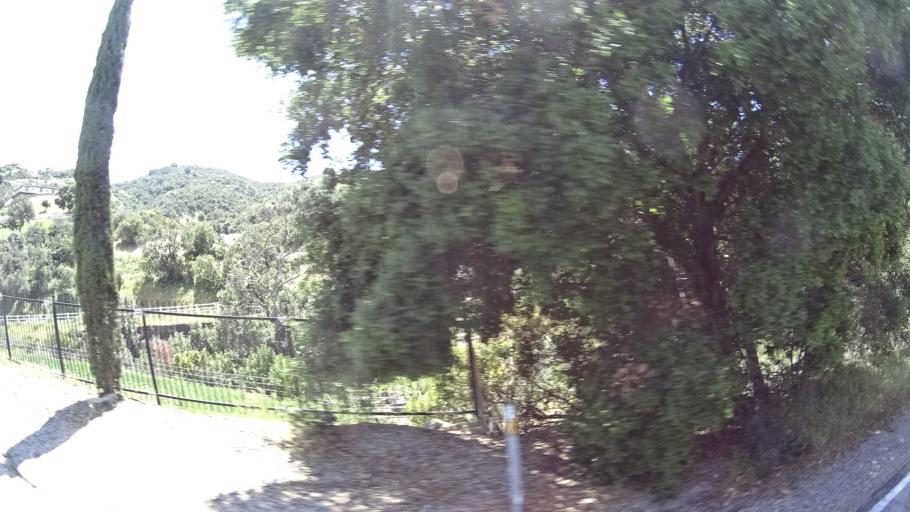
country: US
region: California
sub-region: Ventura County
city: Casa Conejo
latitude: 34.1559
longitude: -118.9388
